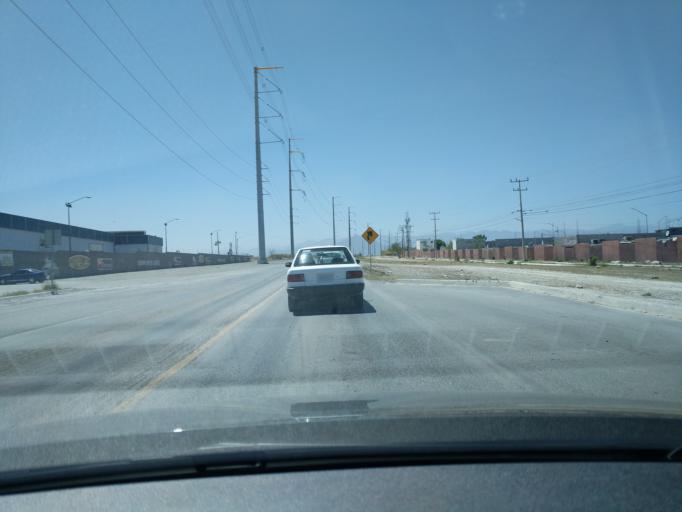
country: MX
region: Nuevo Leon
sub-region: Apodaca
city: Artemio Trevino
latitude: 25.8383
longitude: -100.1376
